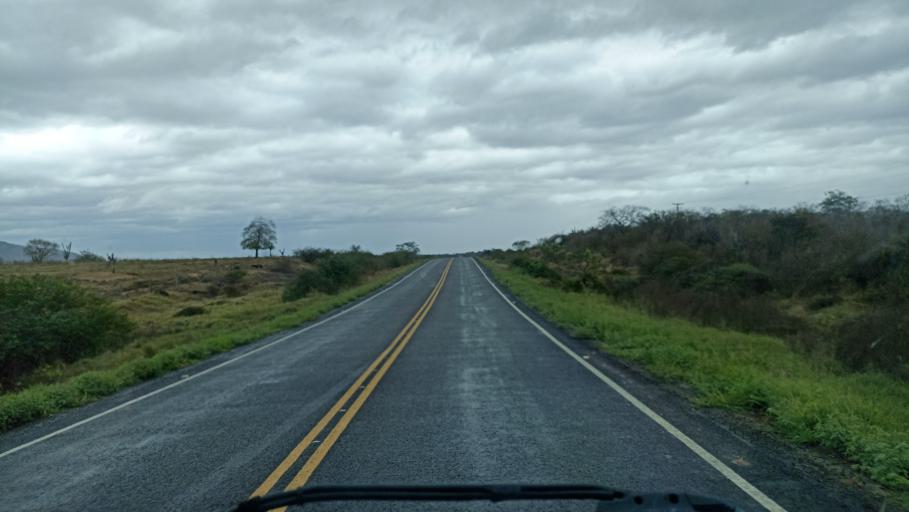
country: BR
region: Bahia
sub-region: Iacu
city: Iacu
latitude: -12.9681
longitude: -40.4945
